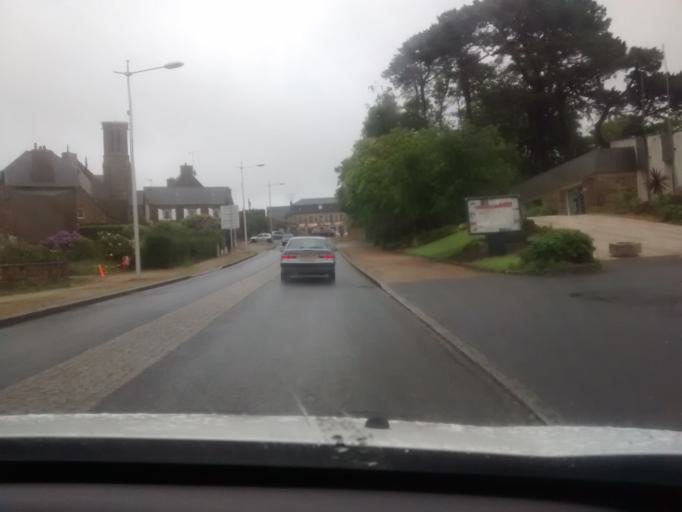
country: FR
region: Brittany
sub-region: Departement des Cotes-d'Armor
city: Louannec
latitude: 48.7948
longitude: -3.4133
